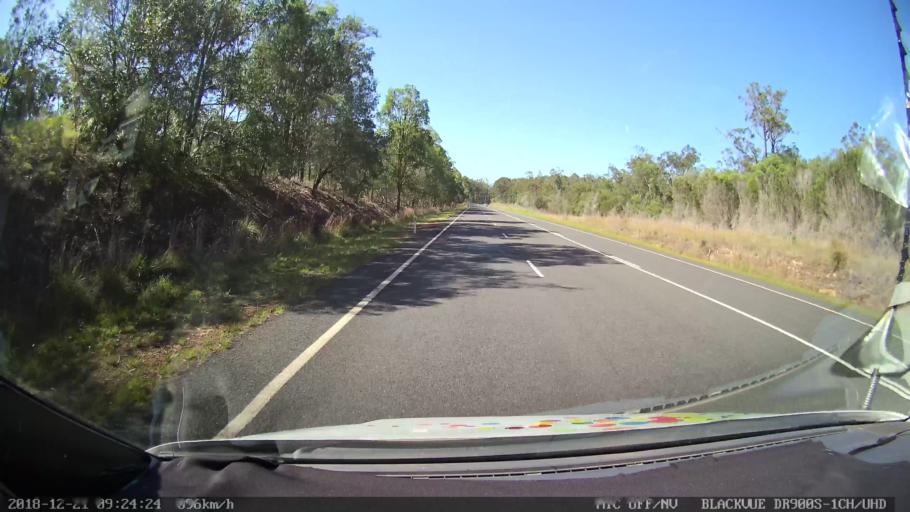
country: AU
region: New South Wales
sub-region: Clarence Valley
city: Maclean
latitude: -29.3669
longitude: 153.0164
